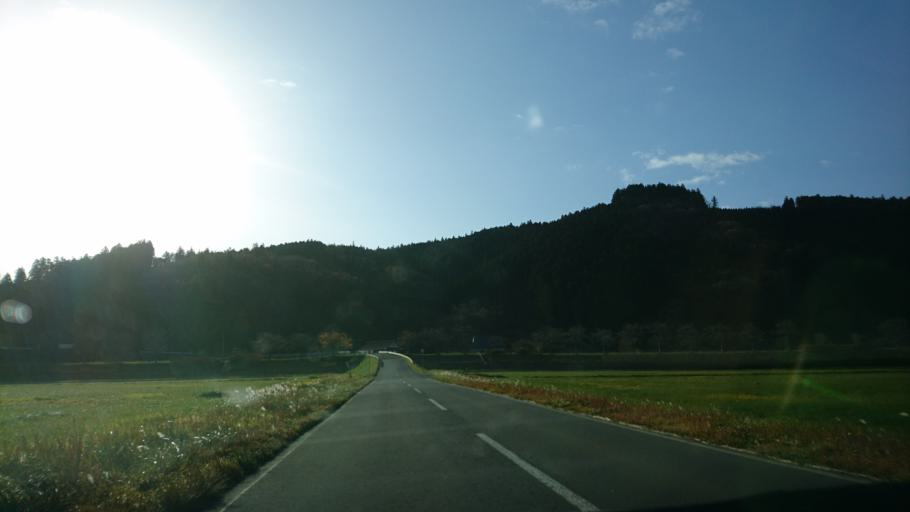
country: JP
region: Iwate
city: Ichinoseki
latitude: 38.8967
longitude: 141.2768
